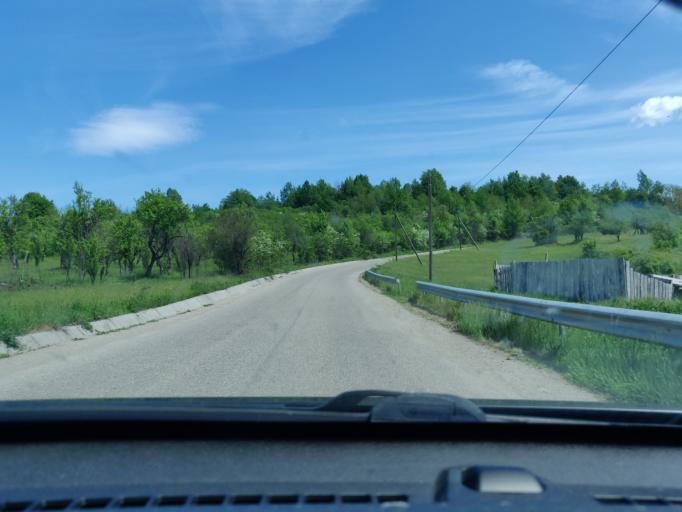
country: RO
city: Vizantea-Manastireasca
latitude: 45.9924
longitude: 26.7761
